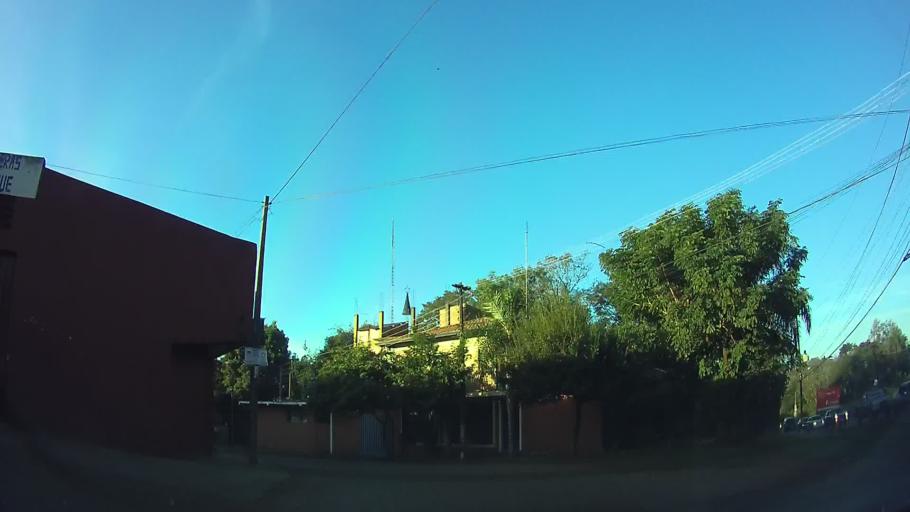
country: PY
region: Central
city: San Lorenzo
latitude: -25.2639
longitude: -57.4835
